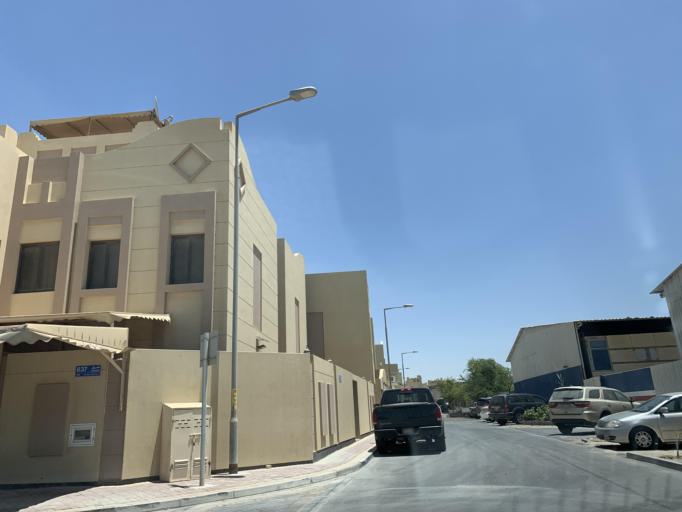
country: BH
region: Manama
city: Jidd Hafs
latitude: 26.2349
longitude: 50.4909
